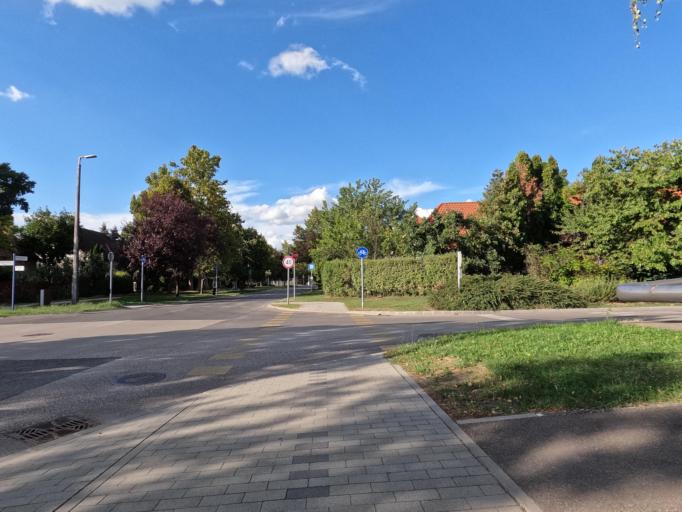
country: HU
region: Tolna
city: Paks
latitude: 46.6134
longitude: 18.8370
